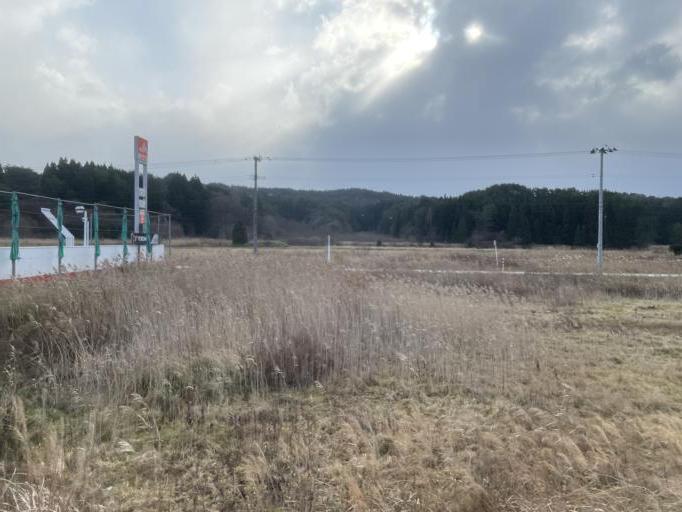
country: JP
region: Aomori
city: Aomori Shi
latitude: 41.0418
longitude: 140.6349
